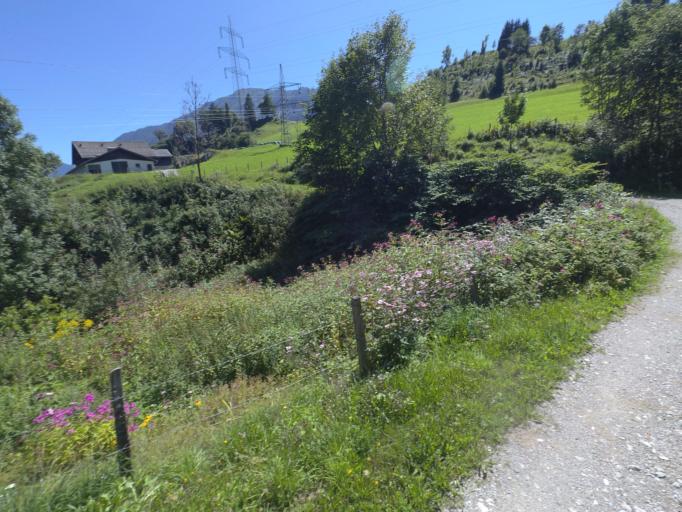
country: AT
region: Salzburg
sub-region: Politischer Bezirk Sankt Johann im Pongau
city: Sankt Veit im Pongau
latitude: 47.3253
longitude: 13.1273
